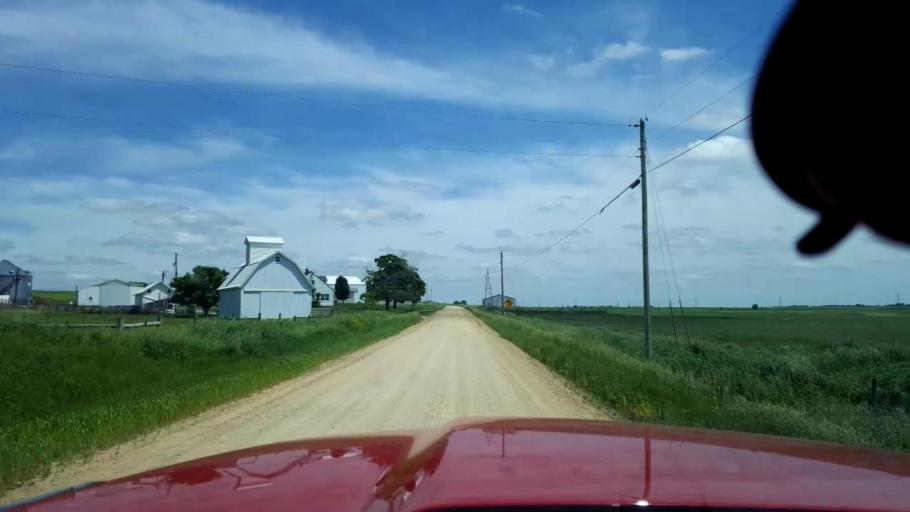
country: US
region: Iowa
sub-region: Linn County
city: Lisbon
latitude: 41.9527
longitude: -91.3566
